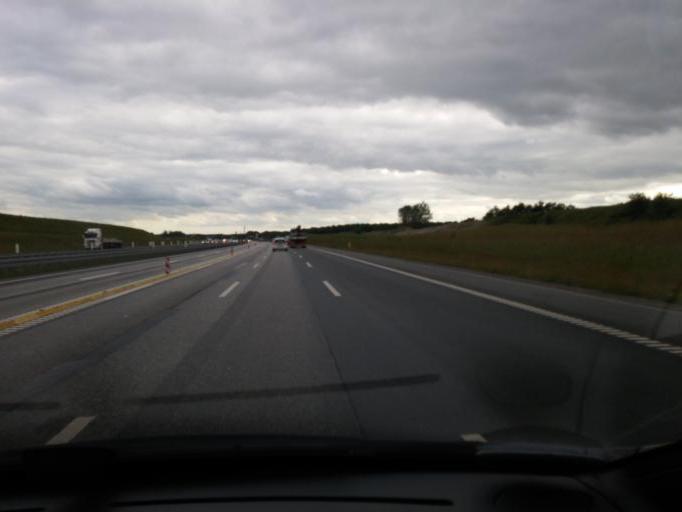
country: DK
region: Zealand
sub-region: Solrod Kommune
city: Solrod Strand
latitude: 55.5677
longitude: 12.2369
